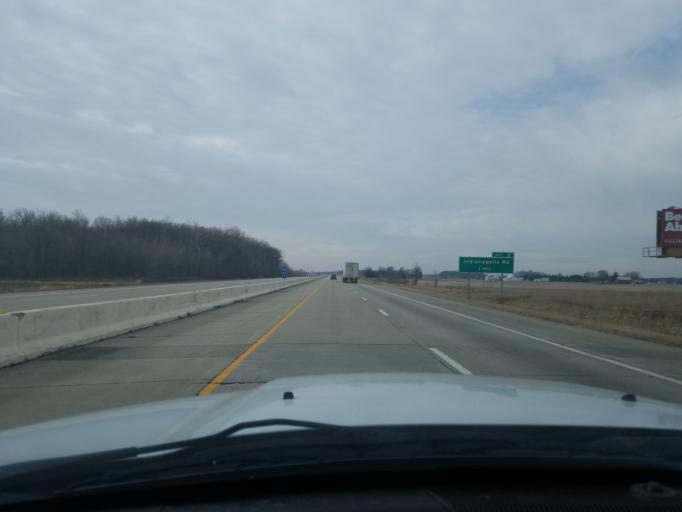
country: US
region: Indiana
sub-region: Wells County
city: Ossian
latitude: 40.9525
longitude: -85.2324
